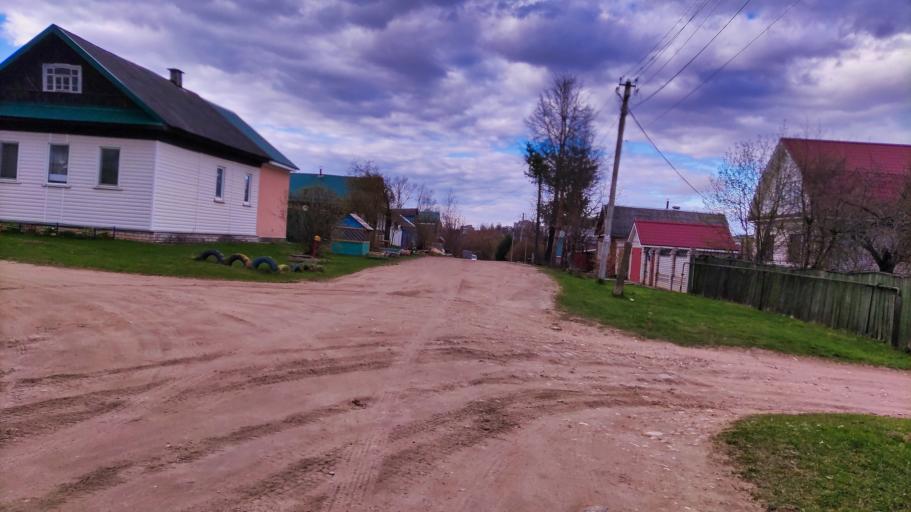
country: RU
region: Tverskaya
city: Rzhev
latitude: 56.2504
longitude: 34.3435
